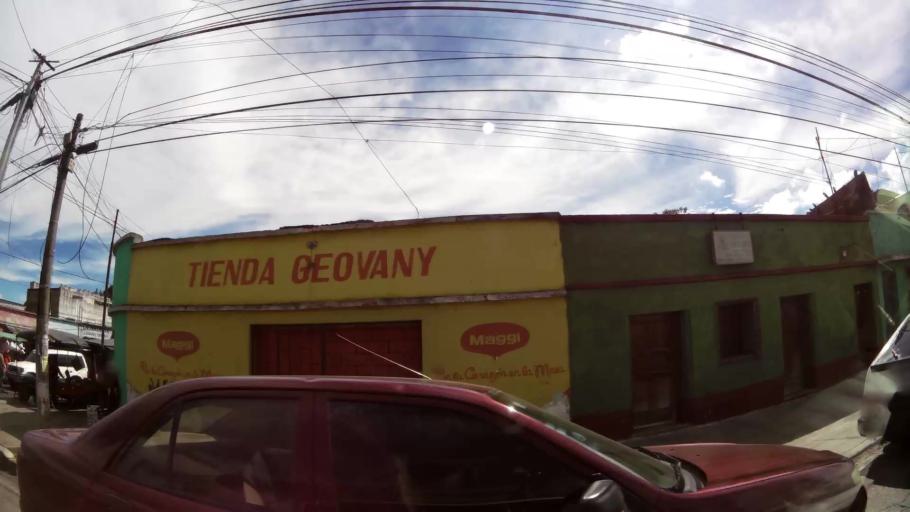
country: GT
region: Guatemala
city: Mixco
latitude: 14.6571
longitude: -90.5792
